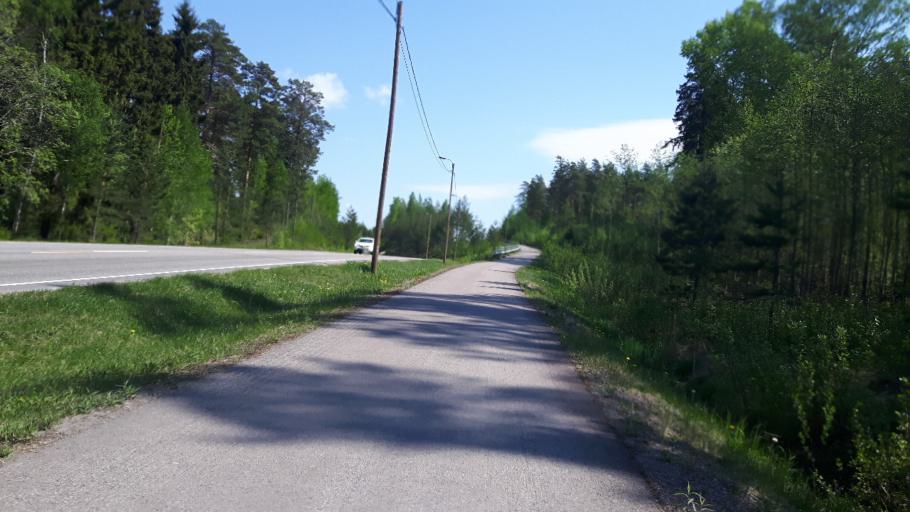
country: FI
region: Uusimaa
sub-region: Loviisa
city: Lovisa
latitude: 60.4630
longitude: 26.2537
